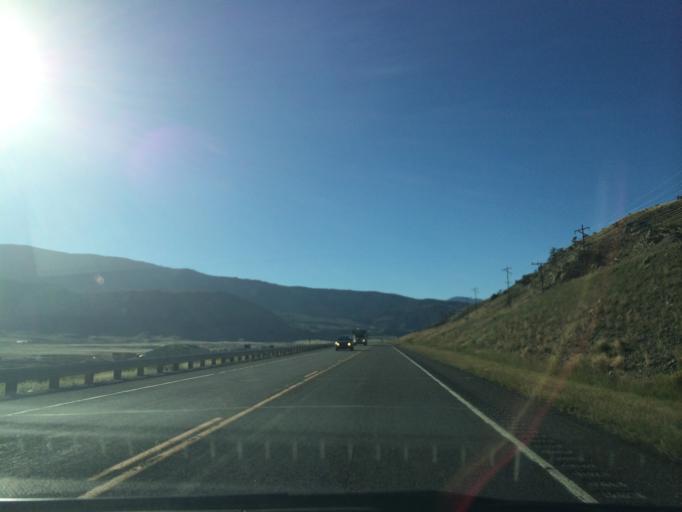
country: US
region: Montana
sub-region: Gallatin County
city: West Yellowstone
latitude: 45.0458
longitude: -110.7343
